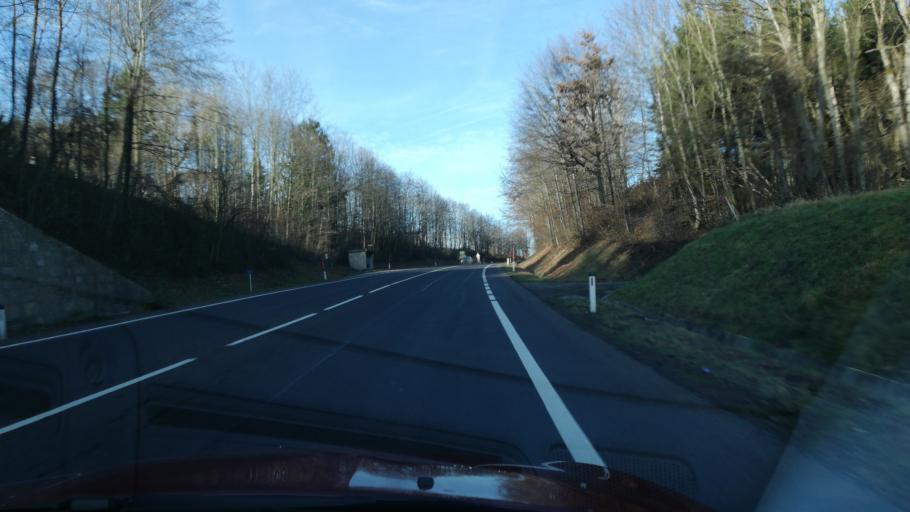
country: AT
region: Upper Austria
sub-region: Politischer Bezirk Kirchdorf an der Krems
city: Micheldorf in Oberoesterreich
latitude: 47.9591
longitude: 14.0806
